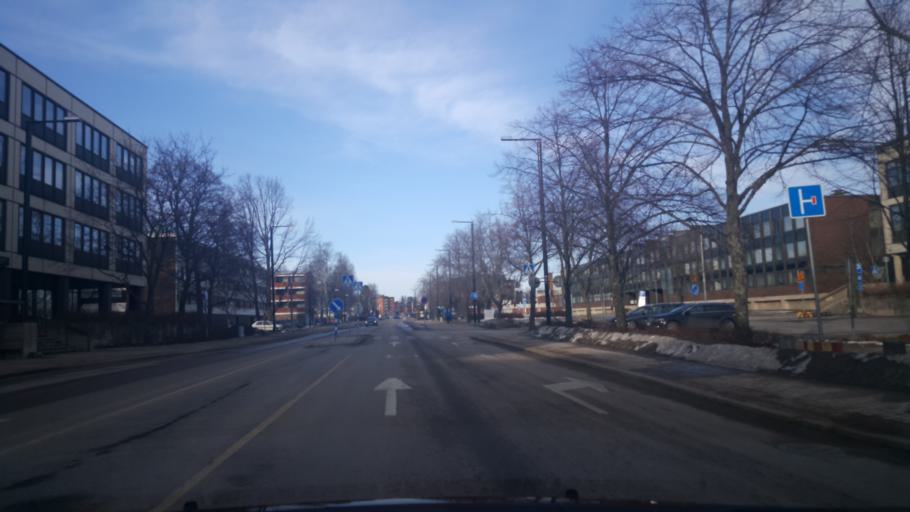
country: FI
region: Uusimaa
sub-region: Helsinki
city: Vantaa
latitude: 60.2942
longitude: 25.0382
